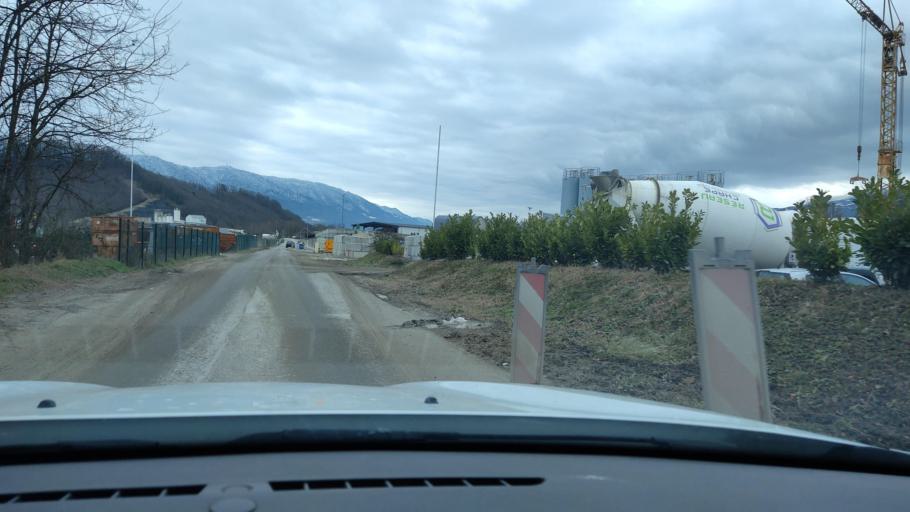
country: FR
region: Rhone-Alpes
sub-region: Departement de la Savoie
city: Montmelian
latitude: 45.4925
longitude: 6.0426
